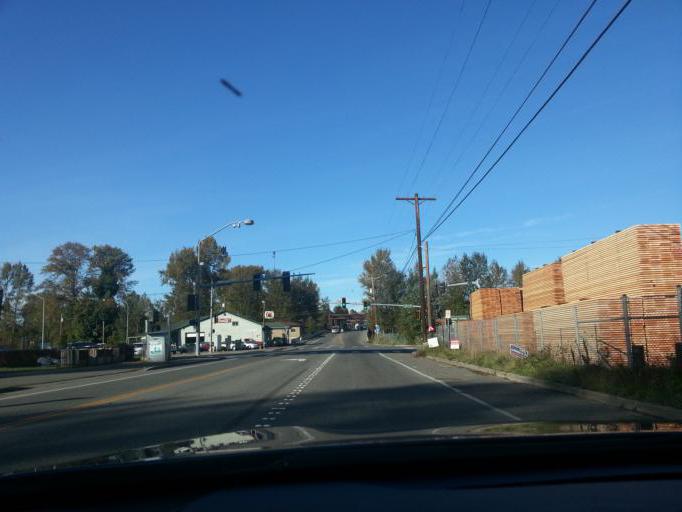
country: US
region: Washington
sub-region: Snohomish County
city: Snohomish
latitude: 47.9086
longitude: -122.0987
